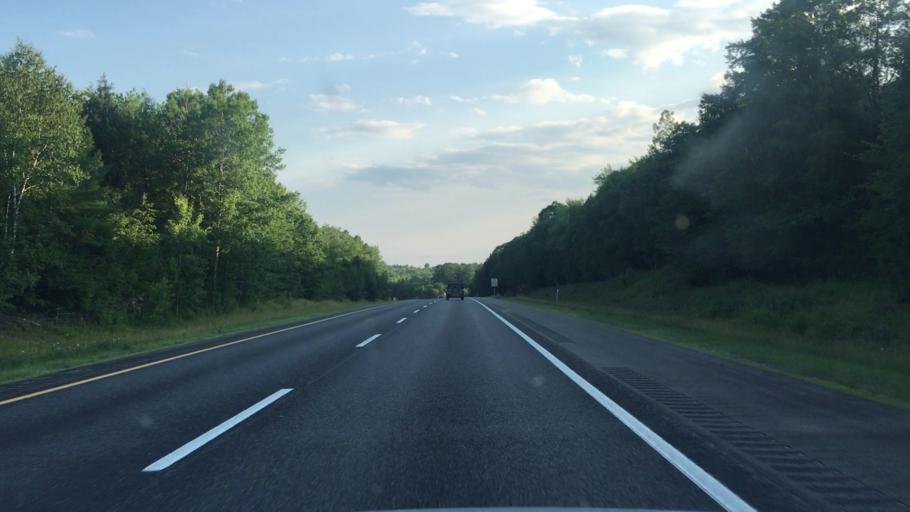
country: US
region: Maine
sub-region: Sagadahoc County
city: Topsham
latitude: 43.9970
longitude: -69.9348
